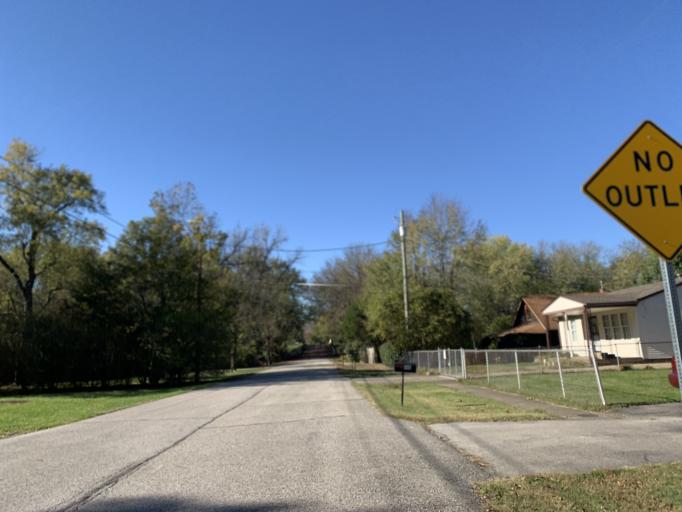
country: US
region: Kentucky
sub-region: Jefferson County
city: Saint Dennis
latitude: 38.1937
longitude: -85.8763
